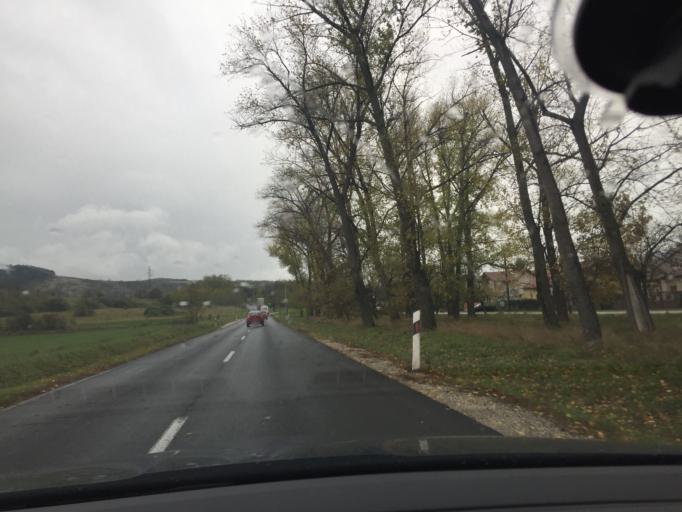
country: HU
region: Komarom-Esztergom
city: Tat
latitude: 47.7334
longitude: 18.6493
